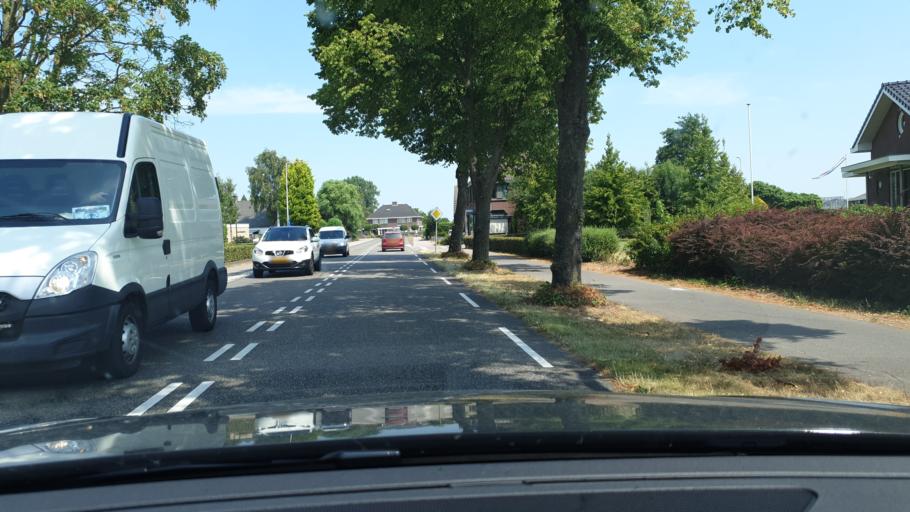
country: NL
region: Gelderland
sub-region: Gemeente Westervoort
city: Westervoort
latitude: 51.9190
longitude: 5.9281
